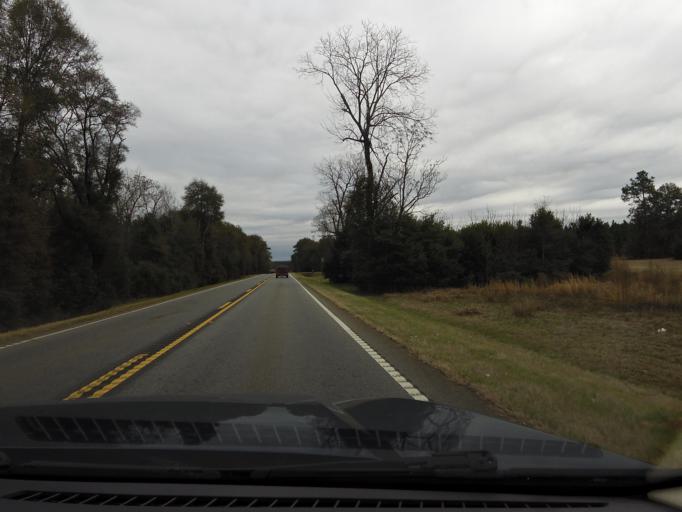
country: US
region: Georgia
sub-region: Randolph County
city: Shellman
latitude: 31.7760
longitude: -84.5725
